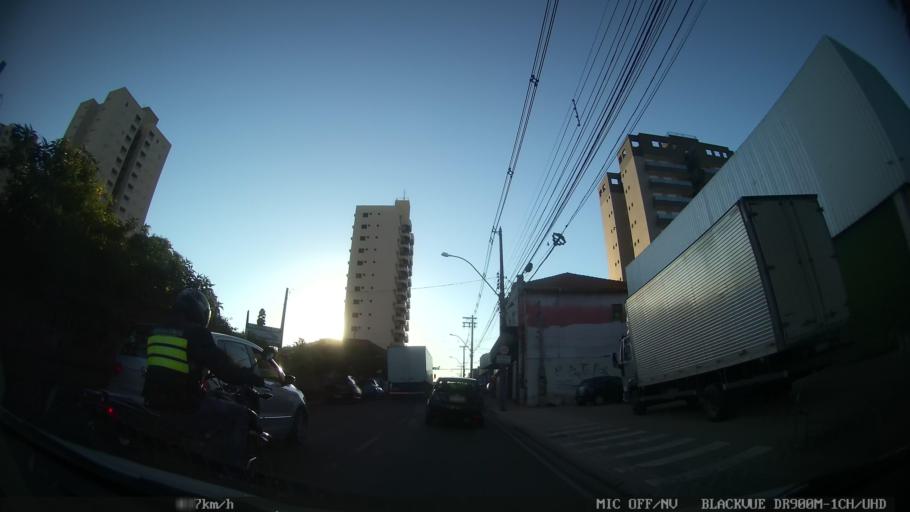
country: BR
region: Sao Paulo
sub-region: Sao Jose Do Rio Preto
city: Sao Jose do Rio Preto
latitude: -20.8060
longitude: -49.3810
